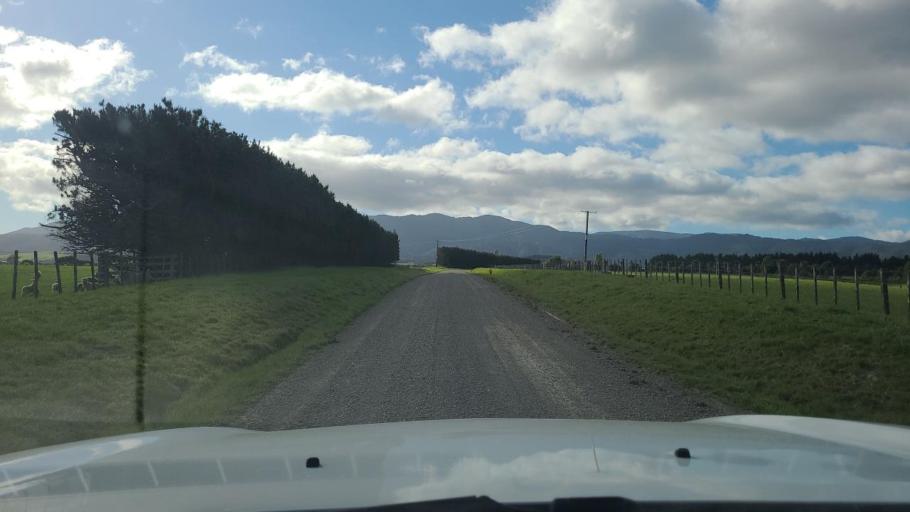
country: NZ
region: Wellington
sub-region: Upper Hutt City
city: Upper Hutt
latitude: -41.3464
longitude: 175.2335
